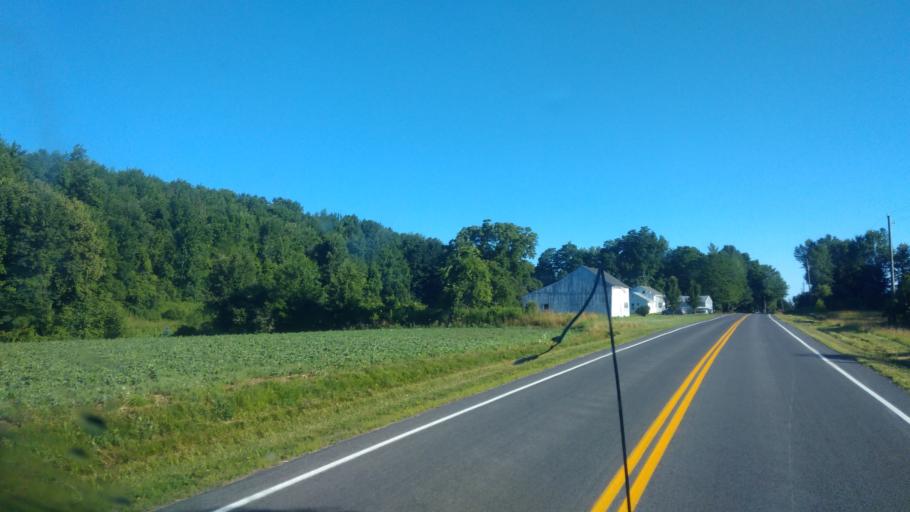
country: US
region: New York
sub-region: Wayne County
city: Sodus
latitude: 43.1578
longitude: -77.0500
